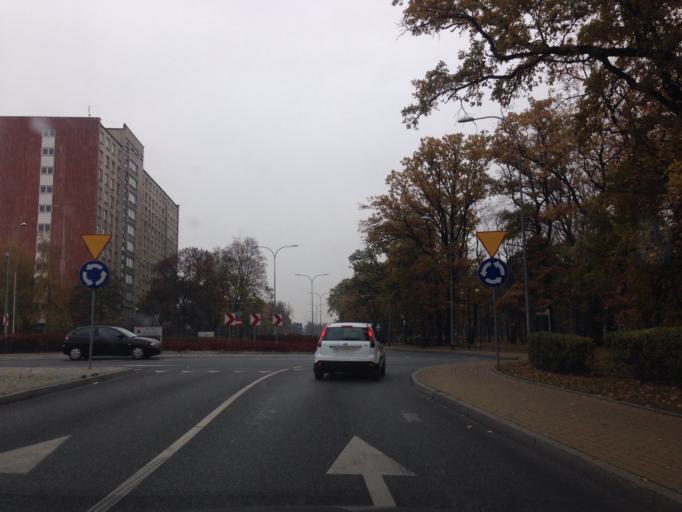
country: PL
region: Kujawsko-Pomorskie
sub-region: Grudziadz
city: Grudziadz
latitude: 53.4772
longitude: 18.7566
